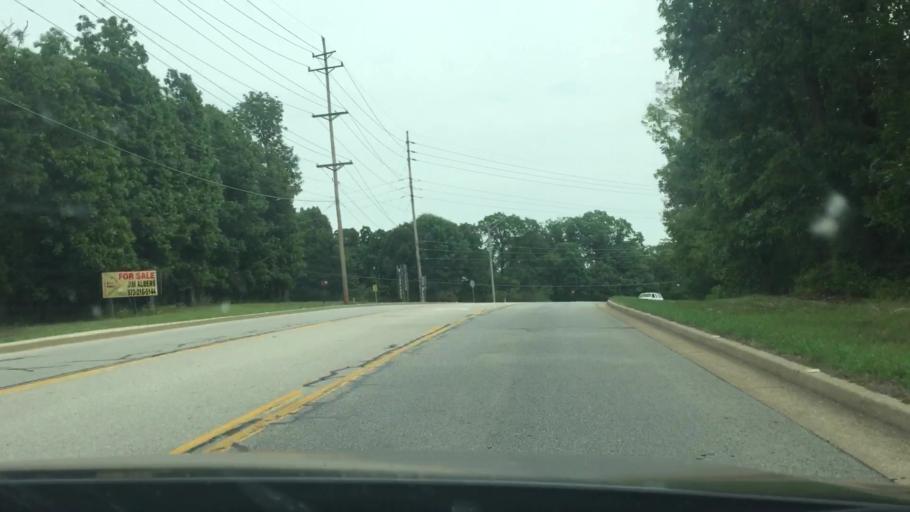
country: US
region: Missouri
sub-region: Camden County
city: Four Seasons
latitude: 38.1949
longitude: -92.6772
